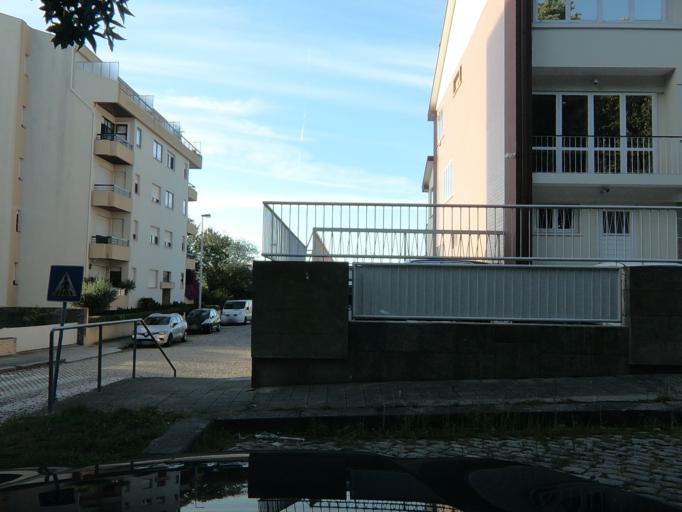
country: PT
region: Porto
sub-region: Matosinhos
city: Sao Mamede de Infesta
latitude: 41.1790
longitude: -8.6184
